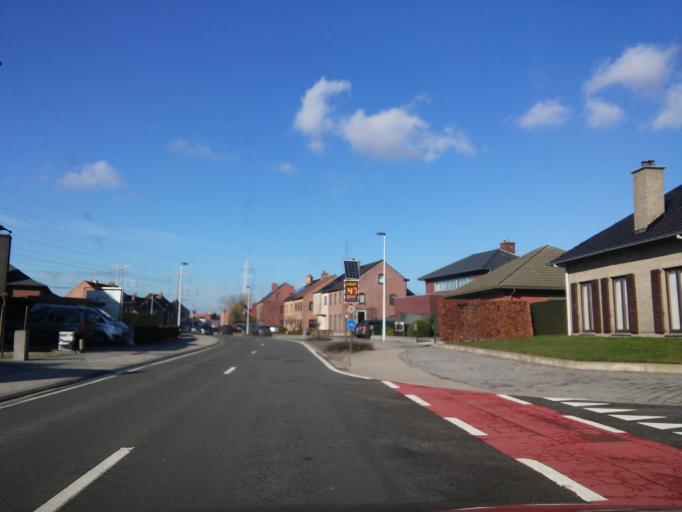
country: BE
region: Flanders
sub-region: Provincie Oost-Vlaanderen
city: Beveren
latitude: 51.1777
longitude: 4.2346
